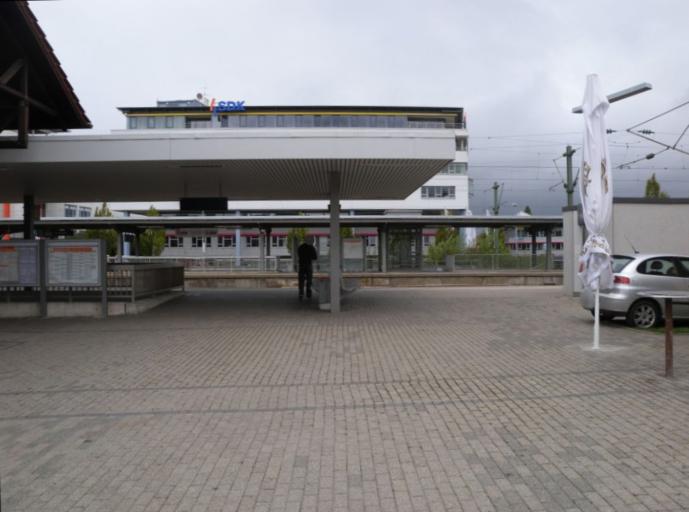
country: DE
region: Baden-Wuerttemberg
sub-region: Regierungsbezirk Stuttgart
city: Fellbach
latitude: 48.8201
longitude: 9.2708
